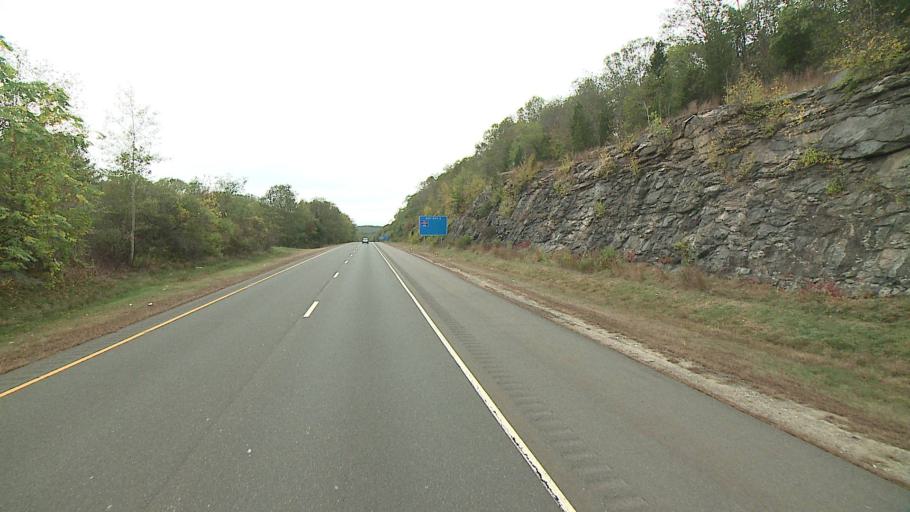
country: US
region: Connecticut
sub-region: Middlesex County
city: Essex Village
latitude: 41.3398
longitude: -72.3966
